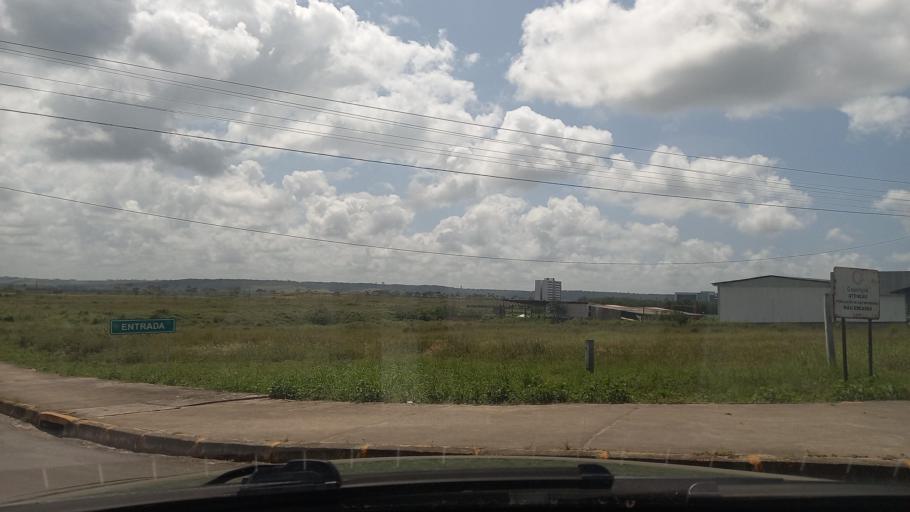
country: BR
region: Pernambuco
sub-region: Goiana
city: Goiana
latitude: -7.5591
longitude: -35.0213
